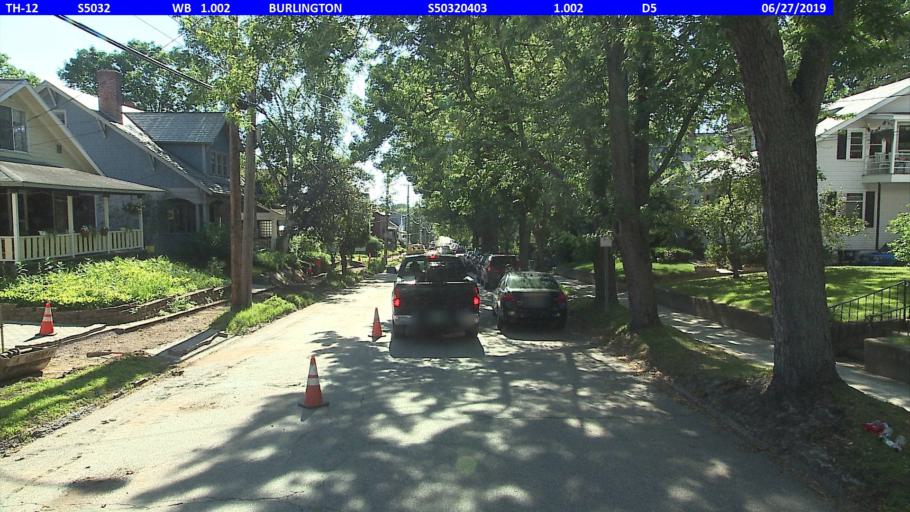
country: US
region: Vermont
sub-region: Chittenden County
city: Burlington
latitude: 44.4850
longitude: -73.2023
